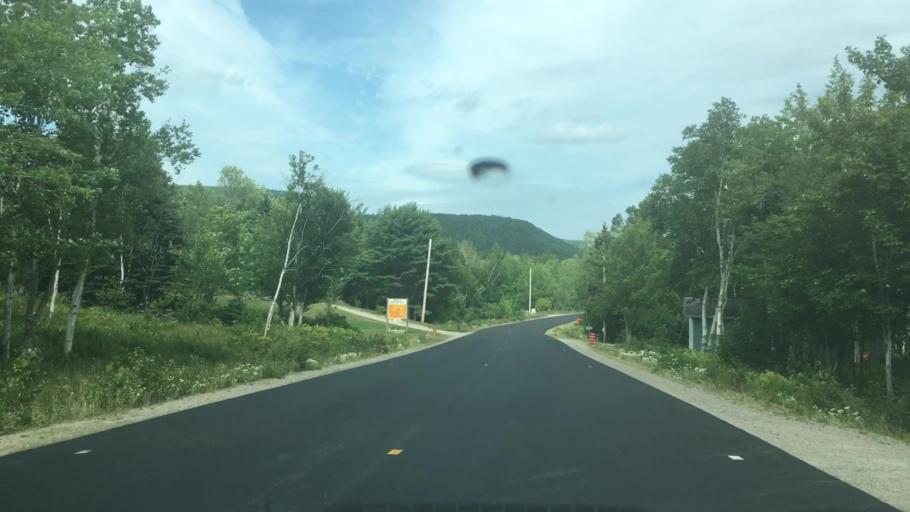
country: CA
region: Nova Scotia
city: Sydney Mines
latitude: 46.5487
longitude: -60.4120
